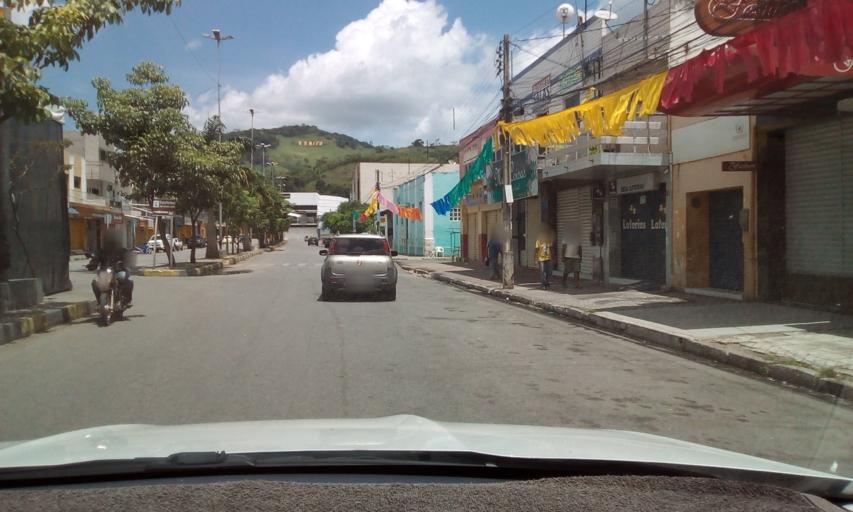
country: BR
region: Pernambuco
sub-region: Bonito
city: Bonito
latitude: -8.4728
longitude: -35.7299
